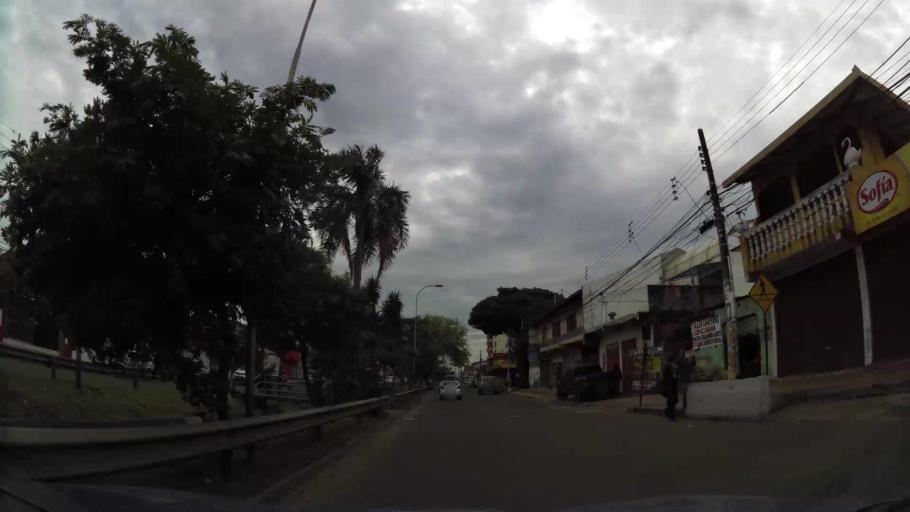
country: BO
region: Santa Cruz
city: Santa Cruz de la Sierra
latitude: -17.7705
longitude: -63.1668
